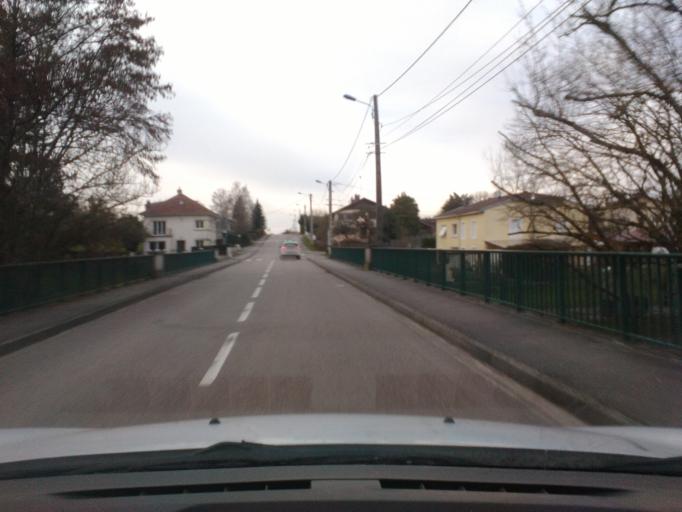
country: FR
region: Lorraine
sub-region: Departement des Vosges
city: Portieux
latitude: 48.3482
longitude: 6.3408
